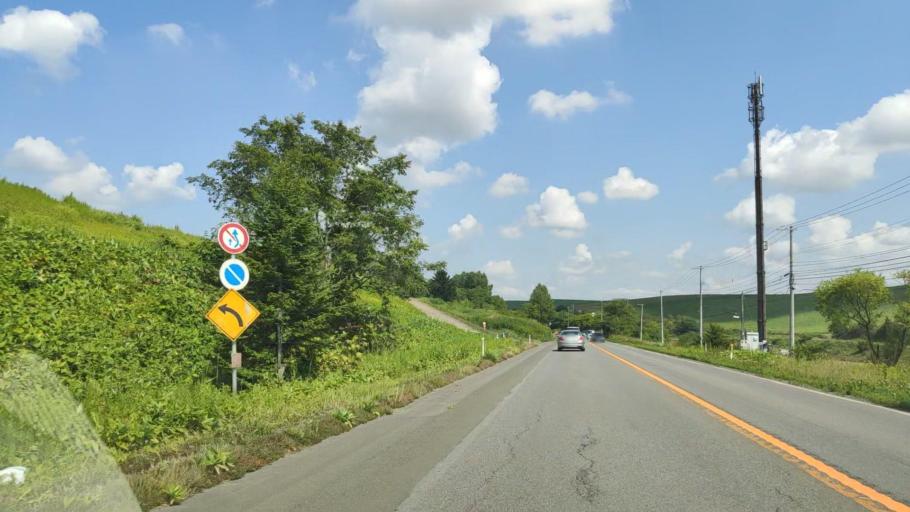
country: JP
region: Hokkaido
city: Shimo-furano
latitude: 43.5490
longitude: 142.4392
